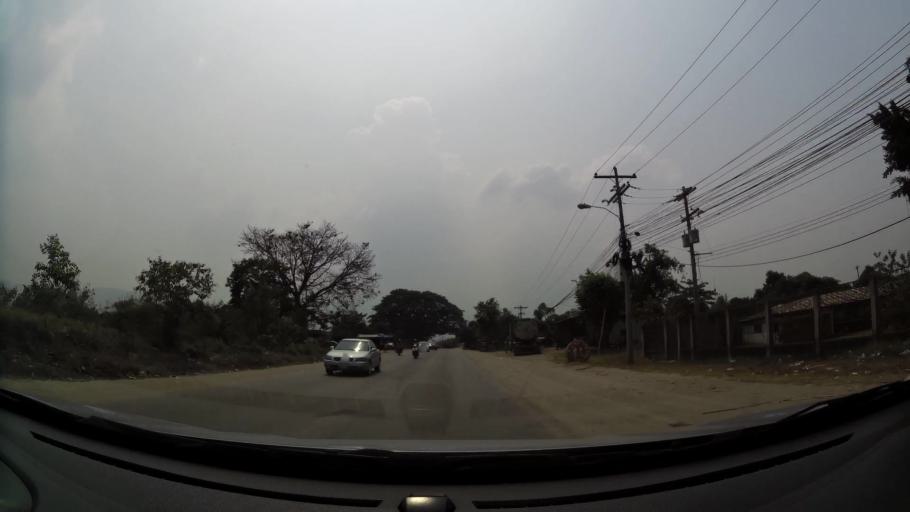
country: HN
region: Cortes
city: San Pedro Sula
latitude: 15.4706
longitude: -87.9941
